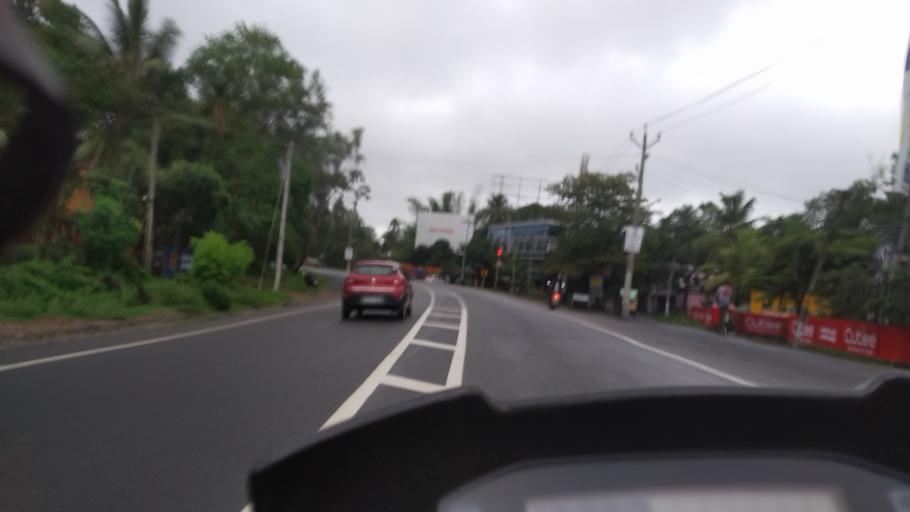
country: IN
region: Kerala
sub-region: Alappuzha
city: Mavelikara
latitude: 9.3178
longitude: 76.4266
